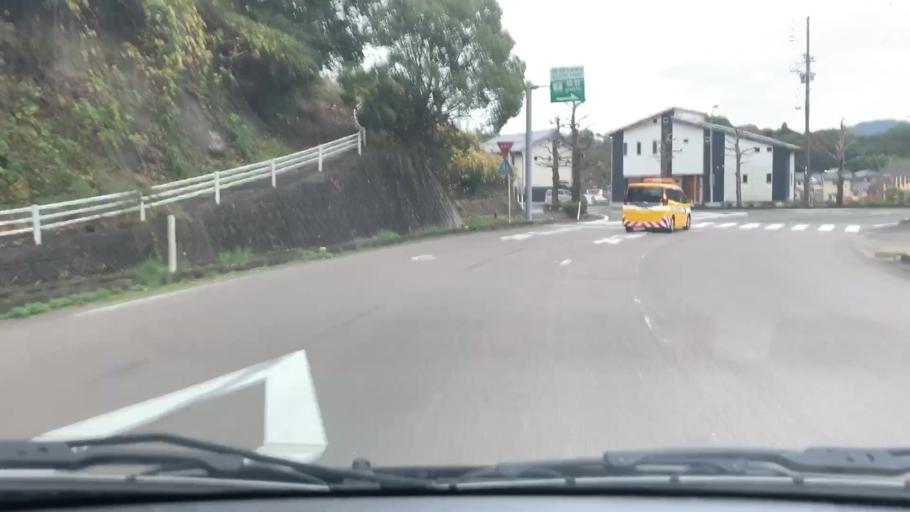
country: JP
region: Saga Prefecture
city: Ureshinomachi-shimojuku
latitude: 33.1084
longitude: 129.9764
